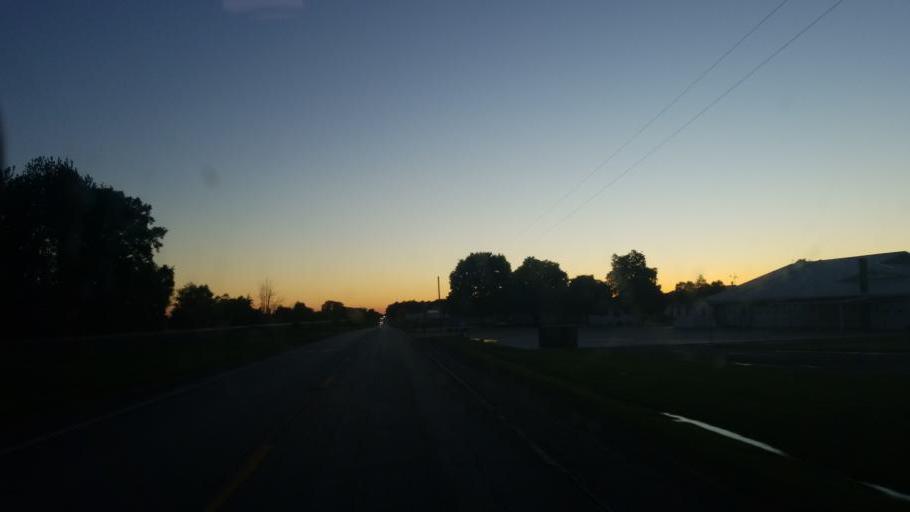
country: US
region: Indiana
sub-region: Elkhart County
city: Nappanee
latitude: 41.4443
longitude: -86.0432
